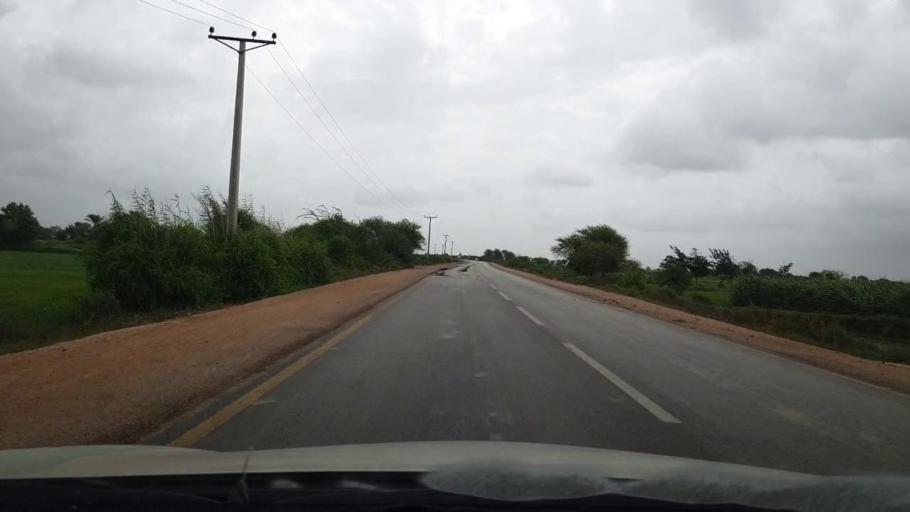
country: PK
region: Sindh
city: Mirpur Batoro
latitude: 24.6210
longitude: 68.3135
